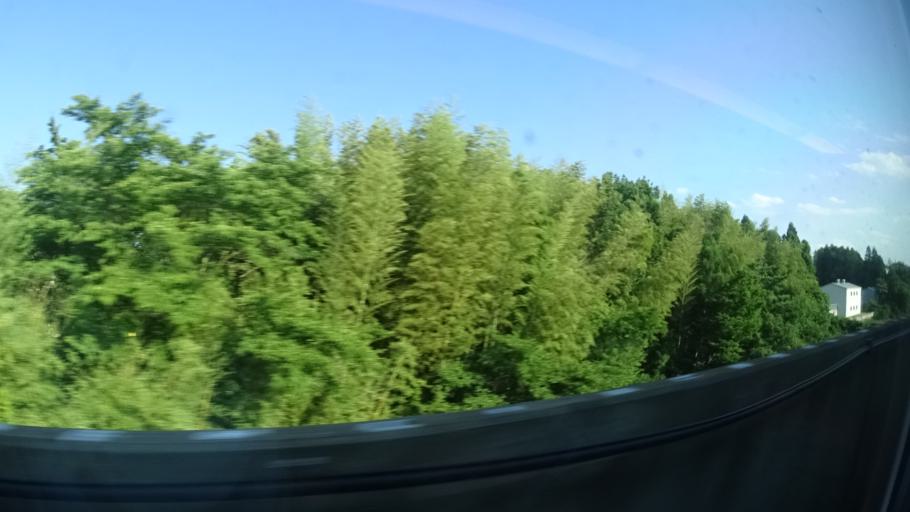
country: JP
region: Fukushima
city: Sukagawa
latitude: 37.3142
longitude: 140.3505
